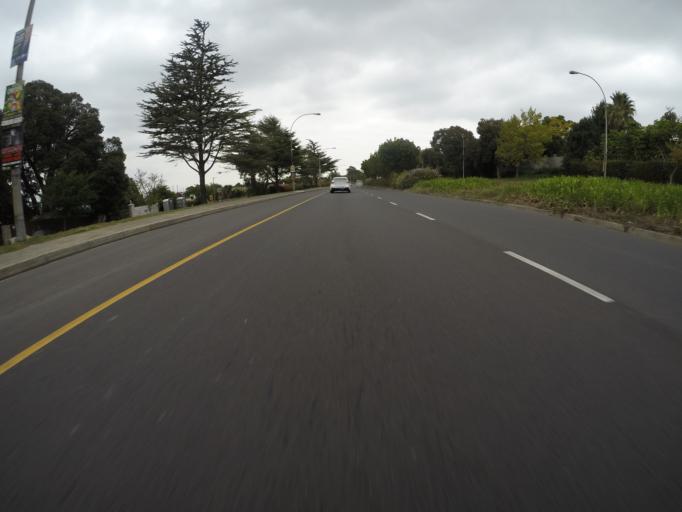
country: ZA
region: Western Cape
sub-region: City of Cape Town
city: Kraaifontein
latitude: -33.8555
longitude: 18.6435
